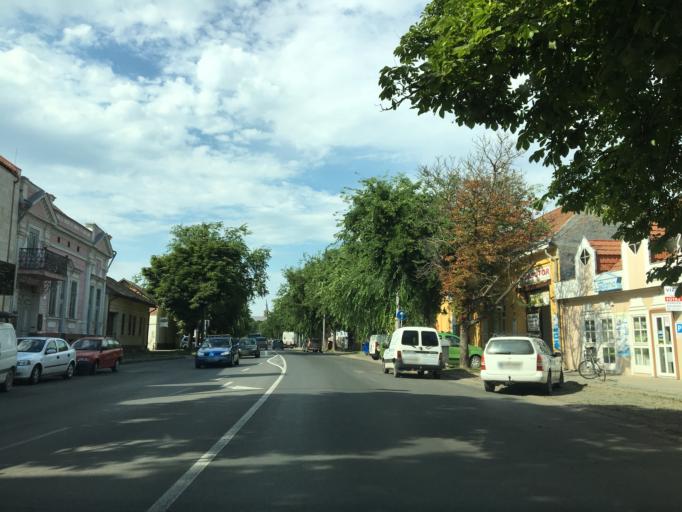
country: HU
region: Tolna
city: Szekszard
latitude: 46.3528
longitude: 18.7030
